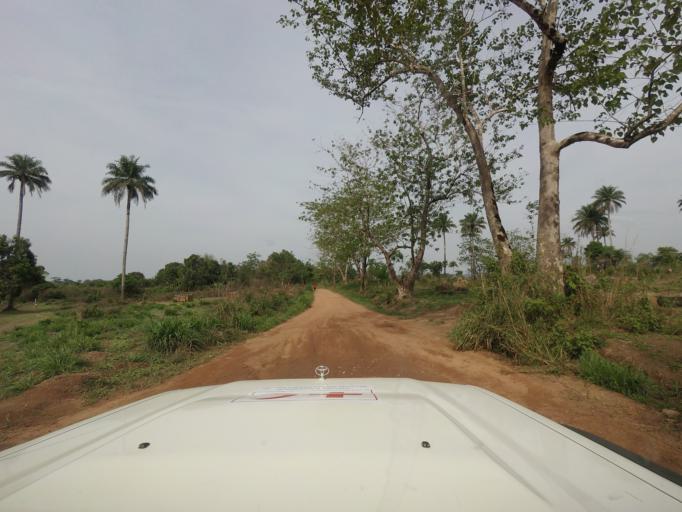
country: GN
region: Nzerekore
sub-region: Macenta
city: Macenta
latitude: 8.5391
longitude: -9.4972
